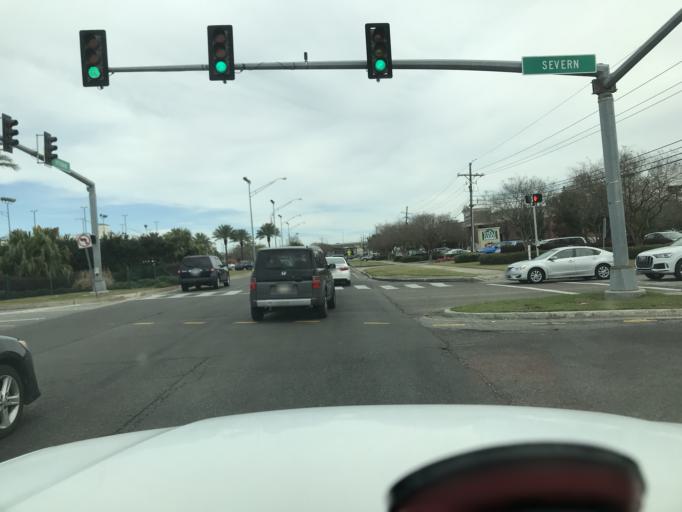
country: US
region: Louisiana
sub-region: Jefferson Parish
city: Metairie
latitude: 30.0033
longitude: -90.1596
